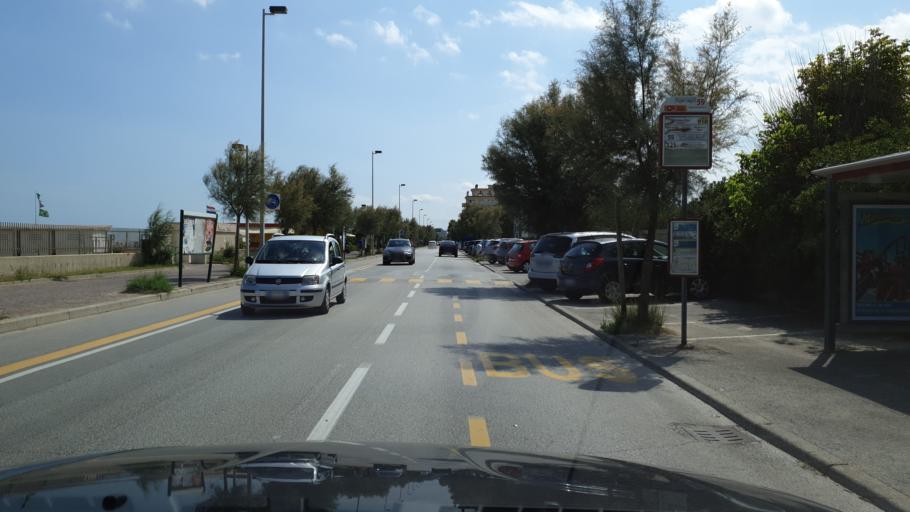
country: IT
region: Emilia-Romagna
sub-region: Provincia di Rimini
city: Misano Adriatico
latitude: 43.9874
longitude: 12.6856
